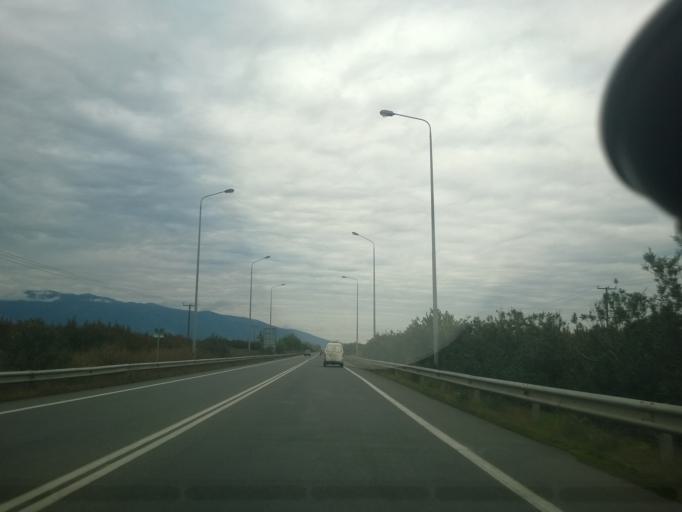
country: GR
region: Central Macedonia
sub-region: Nomos Pellis
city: Mavrovouni
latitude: 40.7893
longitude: 22.1654
